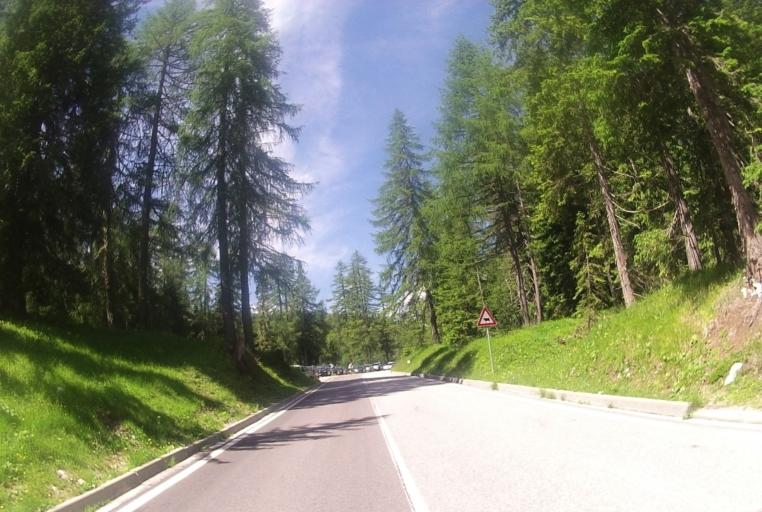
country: IT
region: Veneto
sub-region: Provincia di Belluno
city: Cortina d'Ampezzo
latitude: 46.5564
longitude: 12.2075
